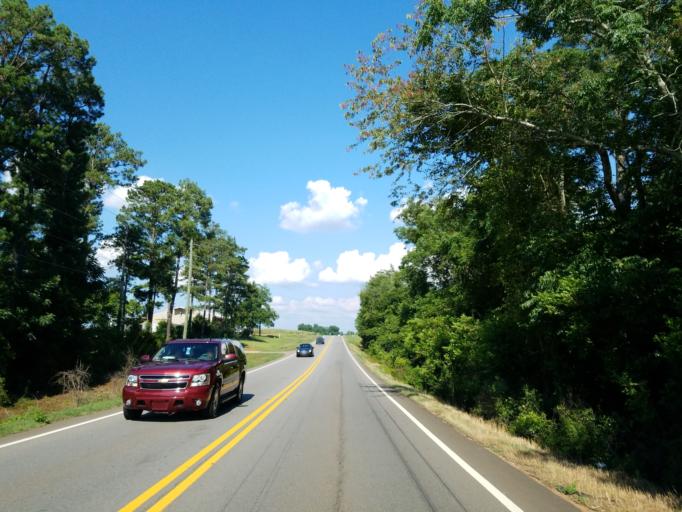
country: US
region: Georgia
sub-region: Peach County
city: Fort Valley
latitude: 32.5538
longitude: -83.7964
